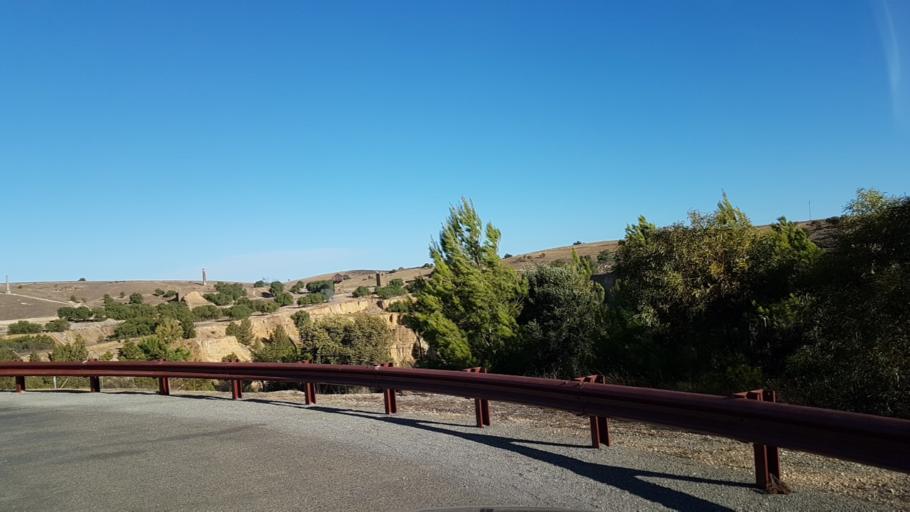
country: AU
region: South Australia
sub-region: Clare and Gilbert Valleys
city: Clare
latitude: -33.6761
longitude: 138.9255
